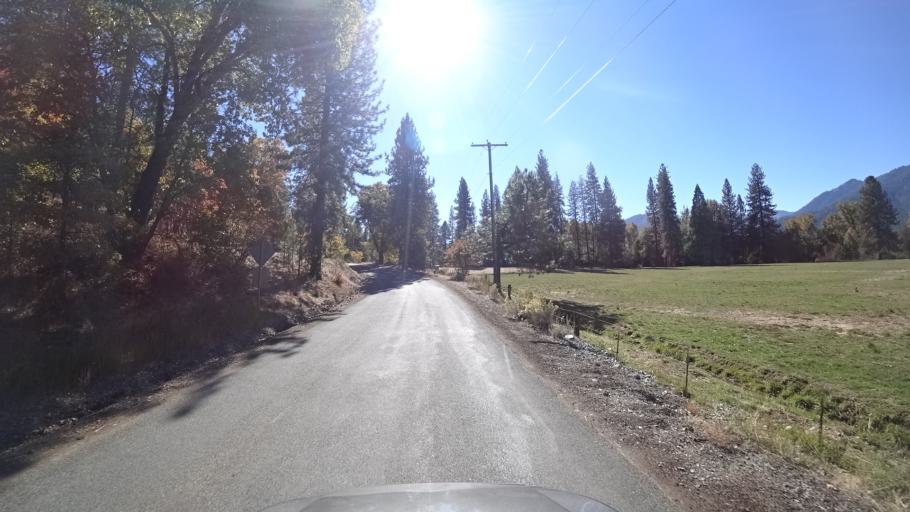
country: US
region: California
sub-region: Siskiyou County
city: Yreka
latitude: 41.5809
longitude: -122.9579
